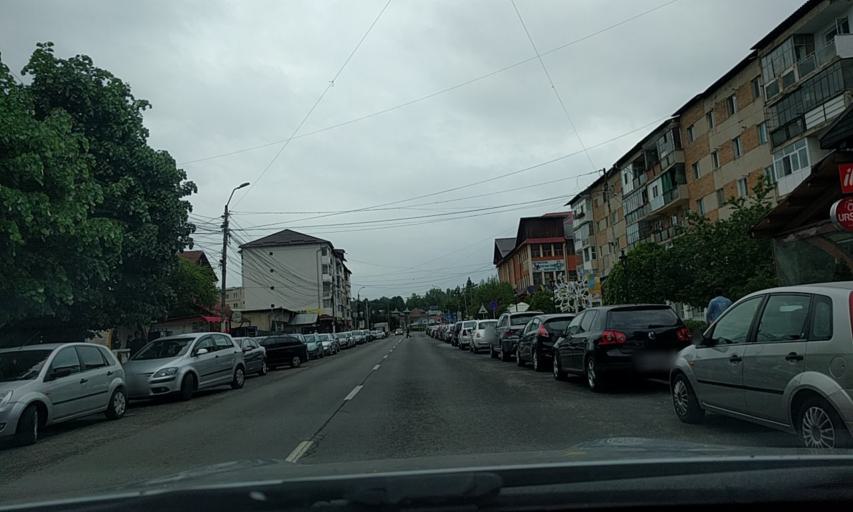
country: RO
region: Dambovita
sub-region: Oras Pucioasa
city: Pucioasa
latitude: 45.0763
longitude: 25.4344
